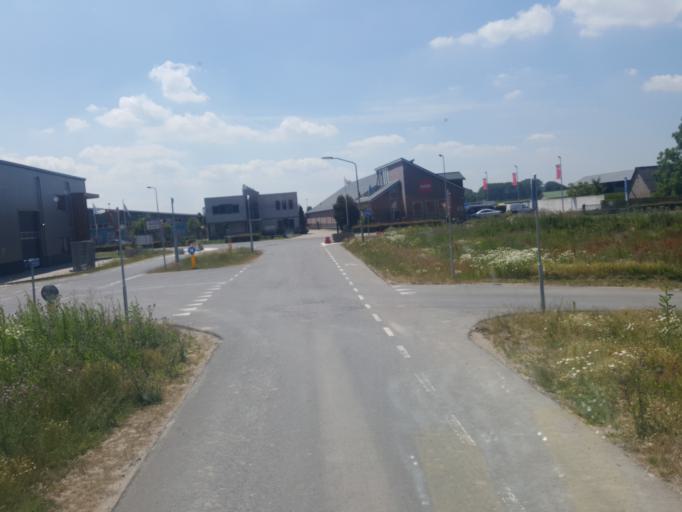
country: NL
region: Gelderland
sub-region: Gemeente Culemborg
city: Culemborg
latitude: 51.8954
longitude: 5.1905
